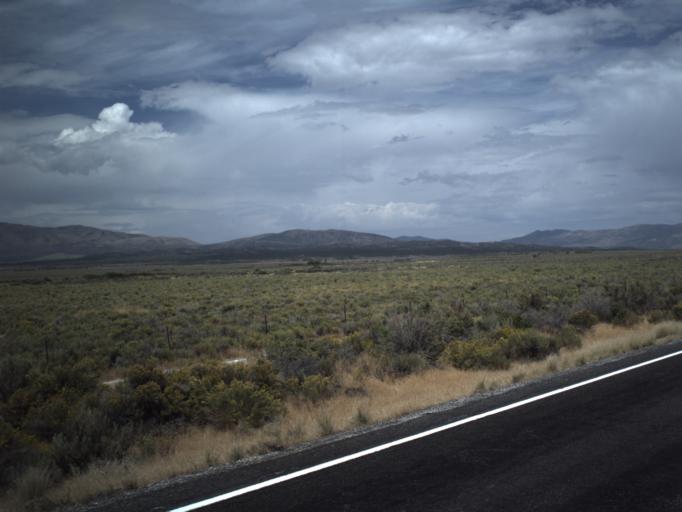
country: US
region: Idaho
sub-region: Cassia County
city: Burley
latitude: 41.6678
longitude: -113.5453
